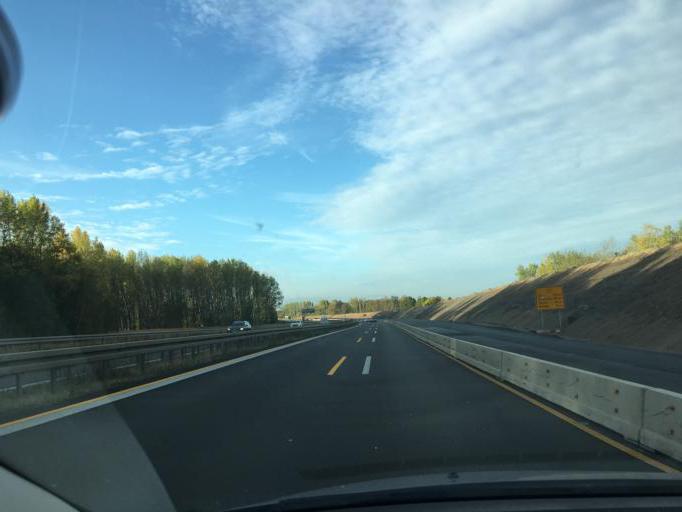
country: DE
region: Saxony
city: Bohlen
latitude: 51.2406
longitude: 12.3918
